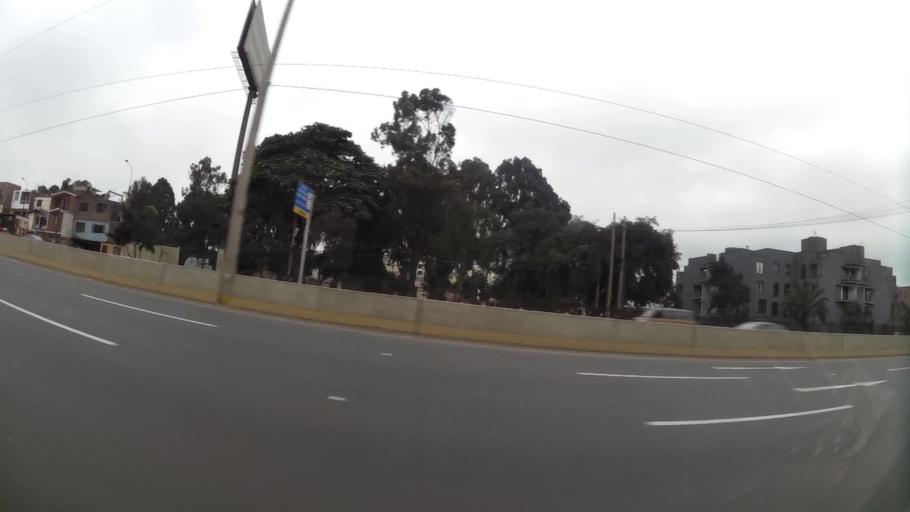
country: PE
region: Lima
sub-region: Lima
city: San Luis
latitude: -12.0779
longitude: -76.9762
